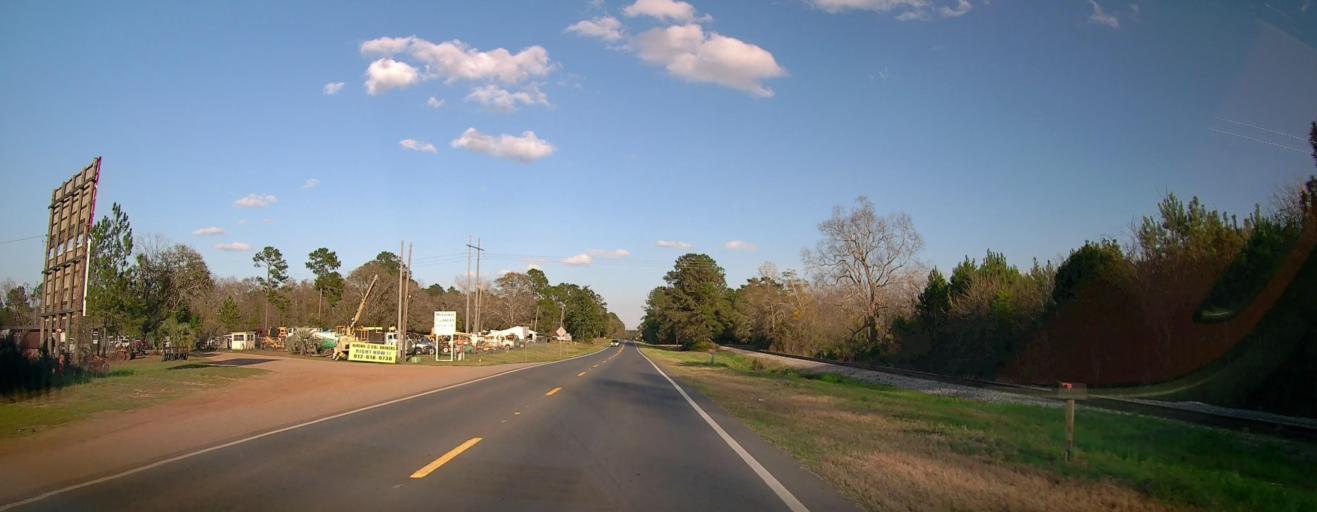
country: US
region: Georgia
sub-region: Evans County
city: Claxton
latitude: 32.1614
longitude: -81.8937
